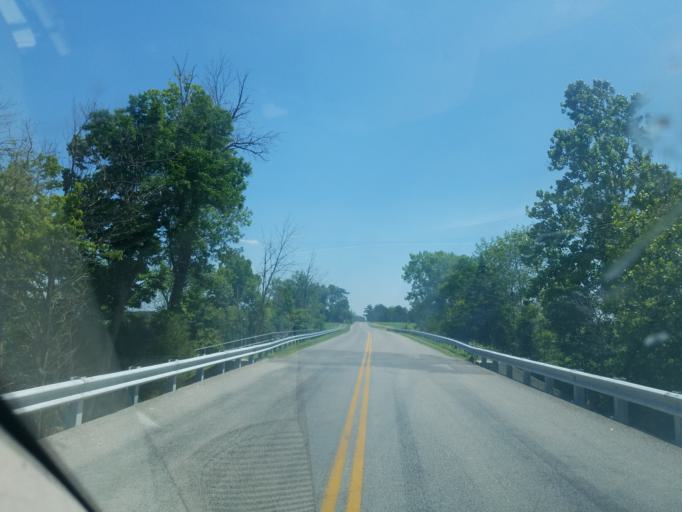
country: US
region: Ohio
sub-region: Allen County
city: Delphos
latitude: 40.7867
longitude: -84.2919
